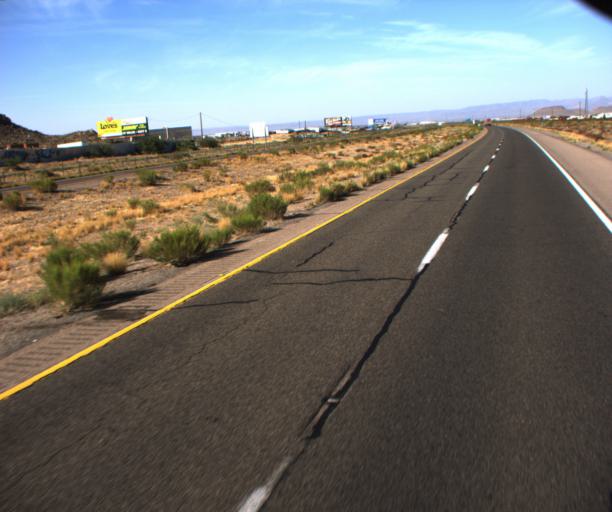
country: US
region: Arizona
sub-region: Mohave County
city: Kingman
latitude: 35.1570
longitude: -114.0847
